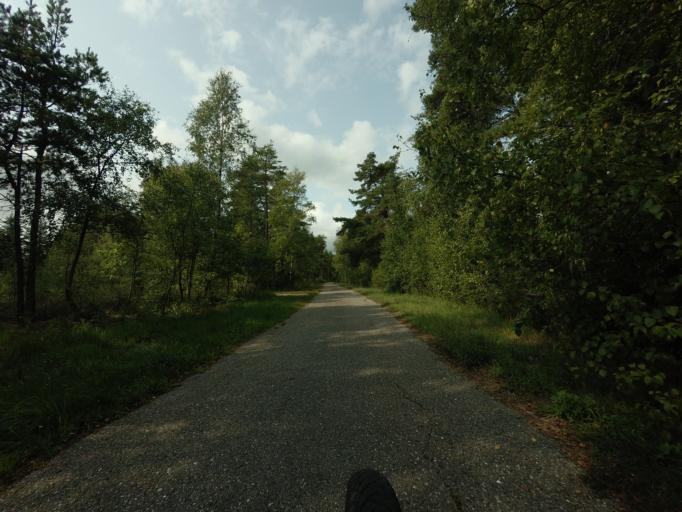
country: DK
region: North Denmark
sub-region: Frederikshavn Kommune
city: Skagen
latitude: 57.6400
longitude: 10.4520
